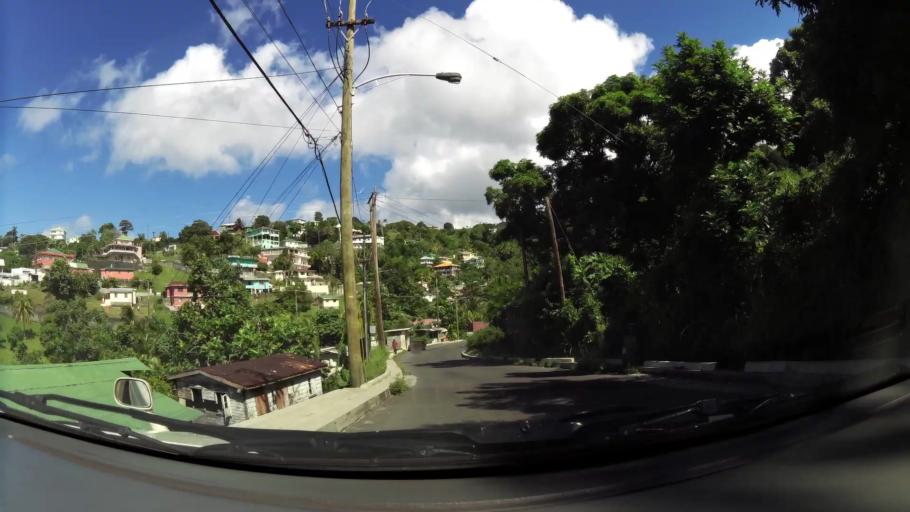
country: VC
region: Saint George
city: Kingstown Park
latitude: 13.1705
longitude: -61.2321
